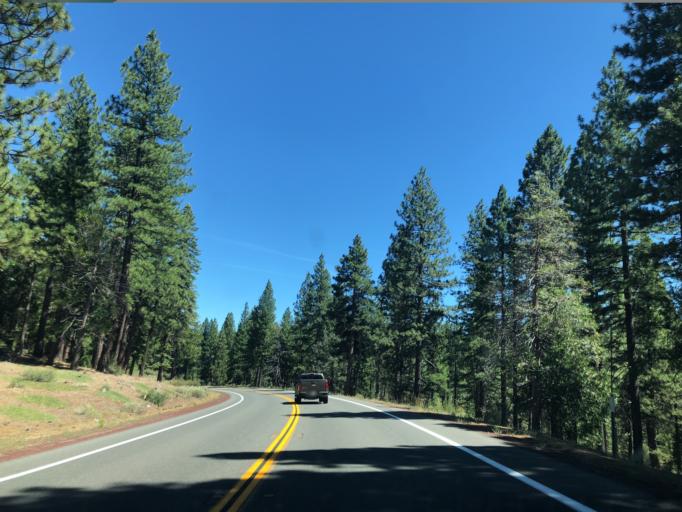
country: US
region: California
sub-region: Lassen County
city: Susanville
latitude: 40.4190
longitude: -120.7848
